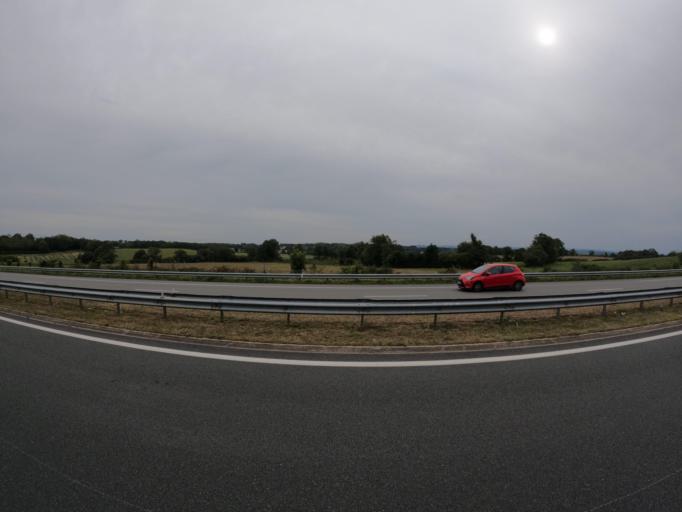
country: FR
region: Limousin
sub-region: Departement de la Creuse
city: Le Grand-Bourg
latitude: 46.2232
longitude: 1.6743
